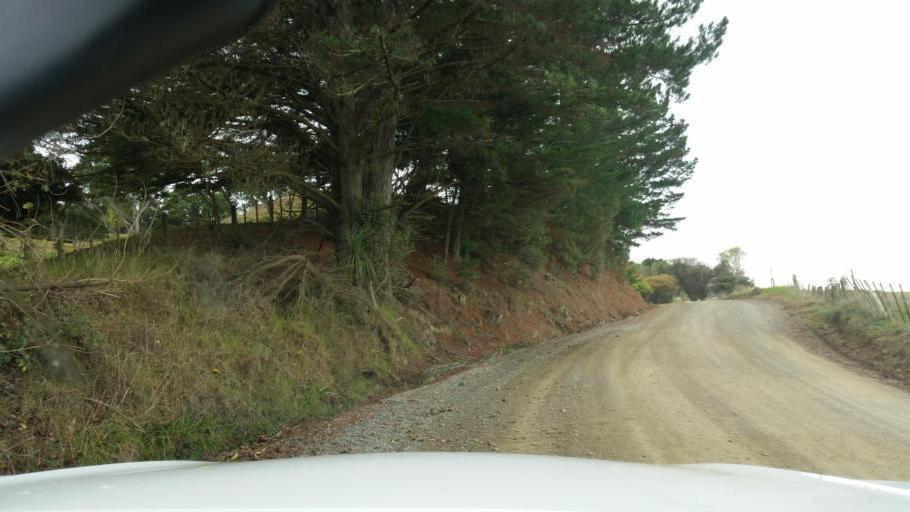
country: NZ
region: Auckland
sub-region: Auckland
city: Wellsford
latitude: -36.1697
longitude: 174.4704
